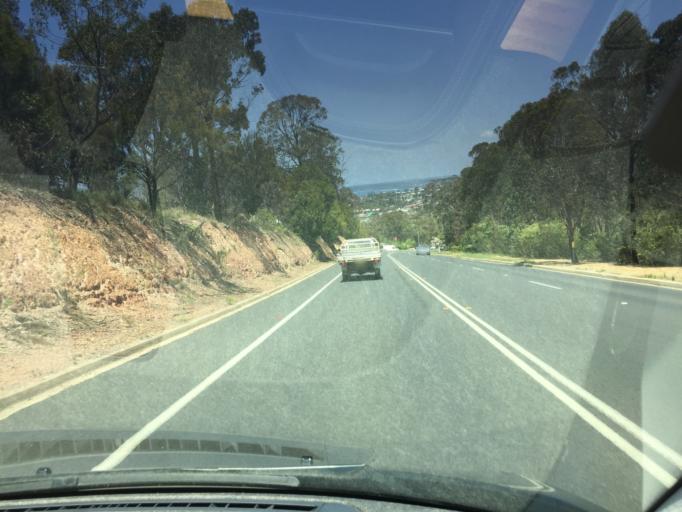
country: AU
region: New South Wales
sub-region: Bega Valley
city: Merimbula
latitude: -36.8779
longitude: 149.9049
